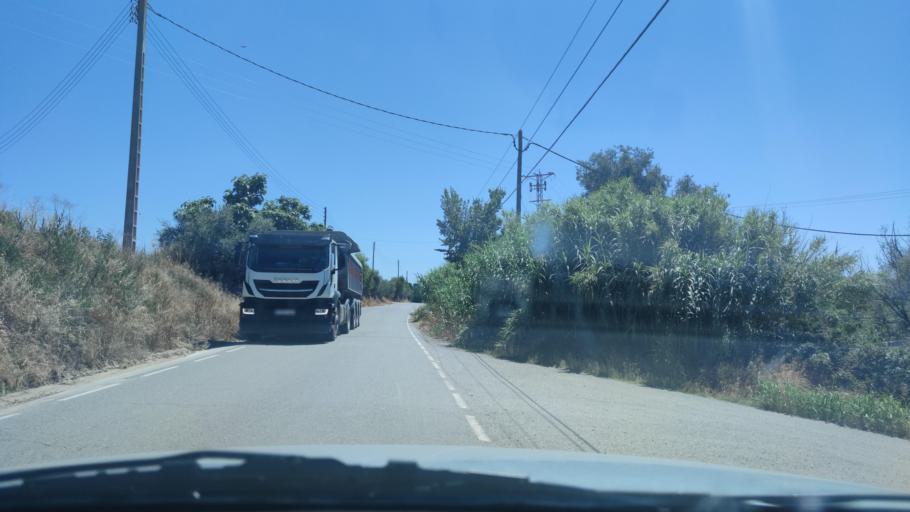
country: ES
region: Catalonia
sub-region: Provincia de Lleida
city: Lleida
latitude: 41.6300
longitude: 0.6557
